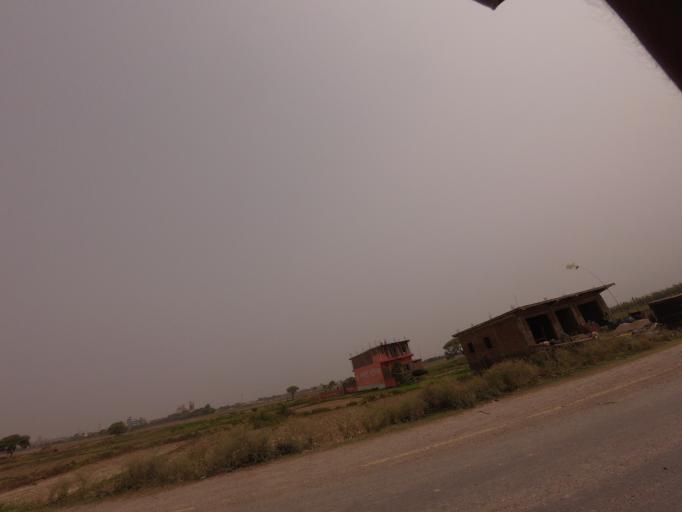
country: NP
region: Western Region
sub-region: Lumbini Zone
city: Bhairahawa
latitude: 27.5066
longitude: 83.3845
